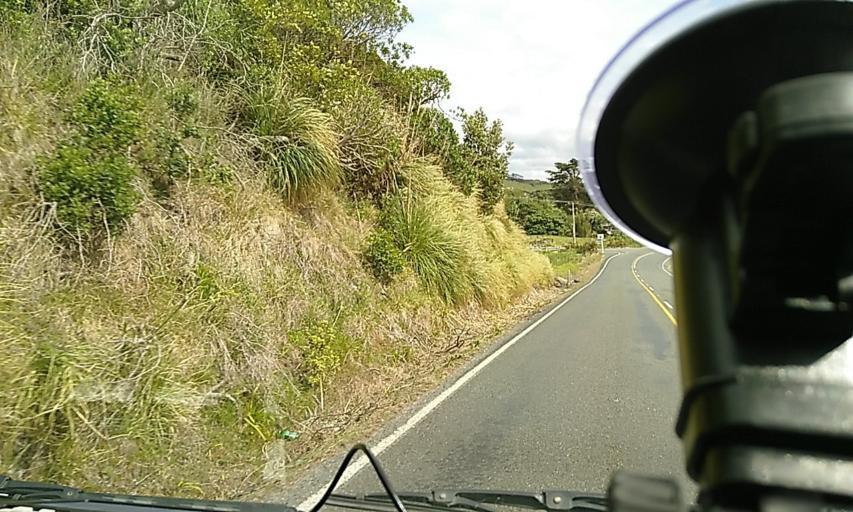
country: NZ
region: Northland
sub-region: Far North District
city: Ahipara
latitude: -35.5153
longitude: 173.3890
